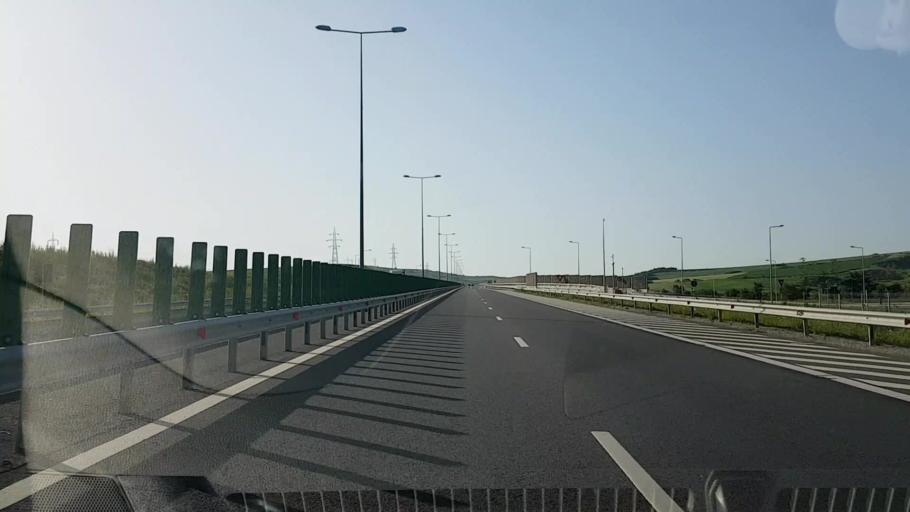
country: RO
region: Alba
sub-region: Comuna Unirea
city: Unirea
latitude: 46.4524
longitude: 23.7917
